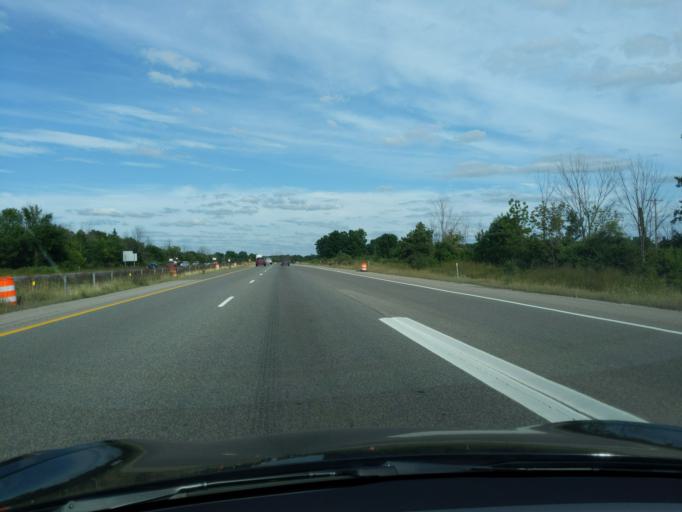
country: US
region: Michigan
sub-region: Muskegon County
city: Fruitport
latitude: 43.0730
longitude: -86.0631
